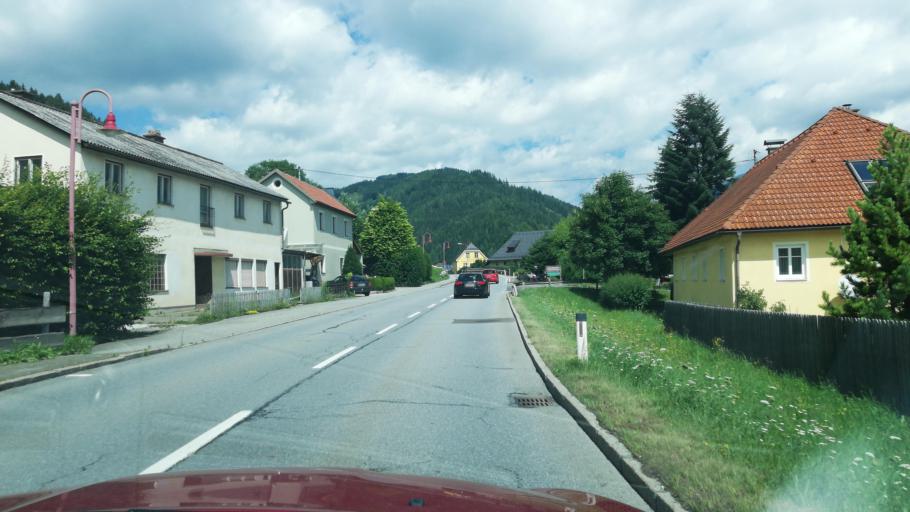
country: AT
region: Styria
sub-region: Politischer Bezirk Murtal
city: Oberzeiring
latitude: 47.2774
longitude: 14.4816
